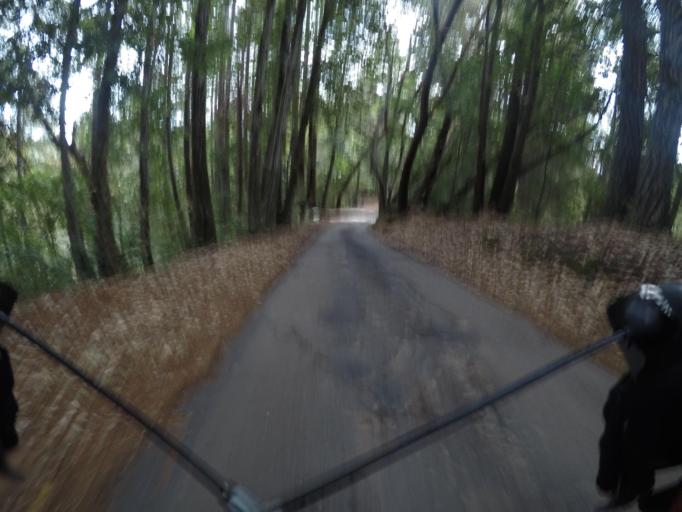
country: US
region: California
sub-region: Santa Cruz County
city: Ben Lomond
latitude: 37.1062
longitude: -122.0876
